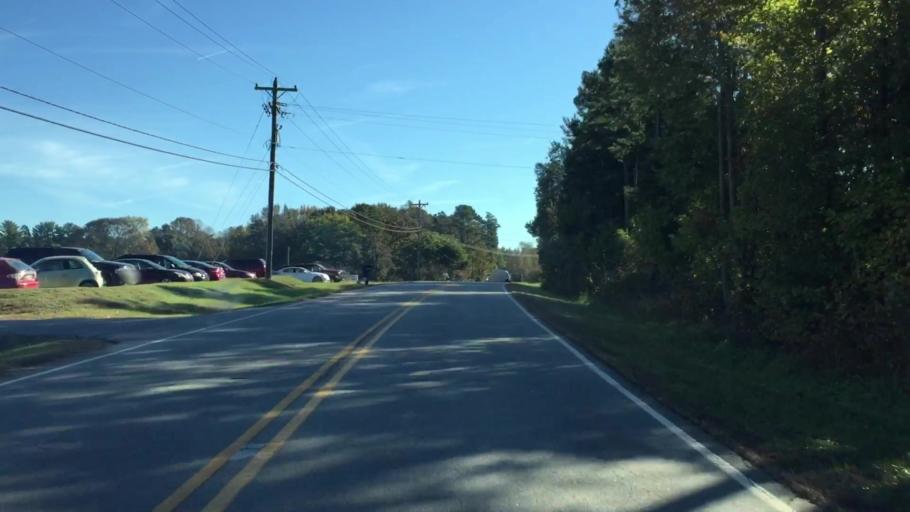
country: US
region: North Carolina
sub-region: Rowan County
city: China Grove
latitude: 35.6507
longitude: -80.6047
